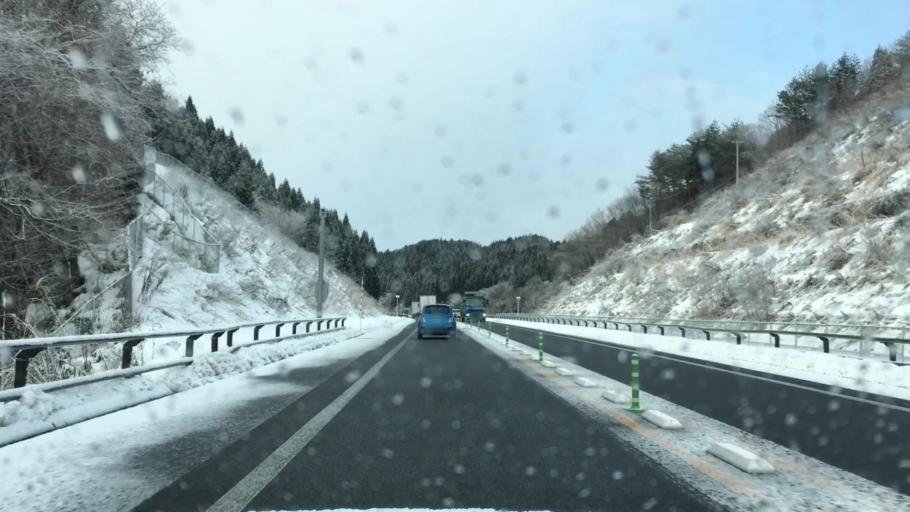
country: JP
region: Akita
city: Takanosu
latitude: 40.2259
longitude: 140.4482
